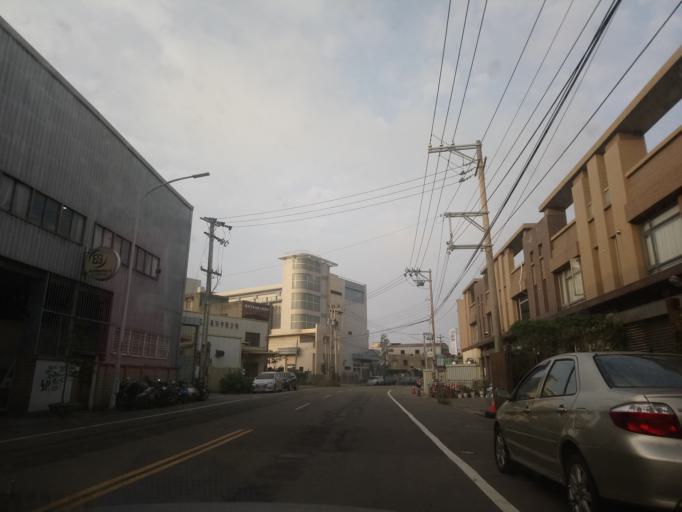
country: TW
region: Taiwan
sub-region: Hsinchu
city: Hsinchu
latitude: 24.7939
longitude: 120.9325
